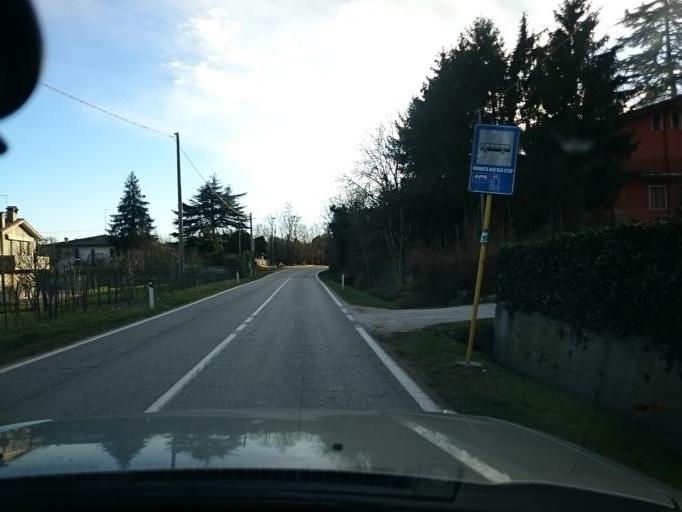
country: IT
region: Veneto
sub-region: Provincia di Padova
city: Torreglia
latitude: 45.3441
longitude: 11.7382
